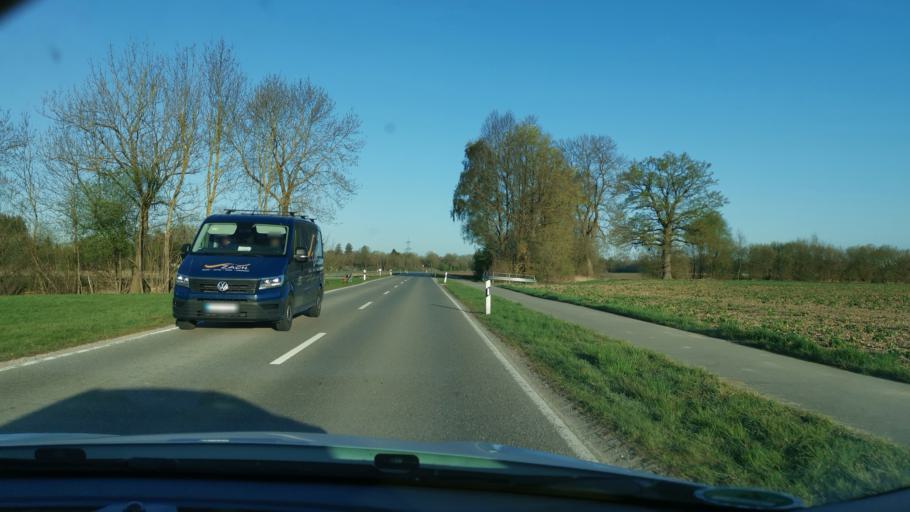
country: DE
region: Bavaria
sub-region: Swabia
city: Langweid
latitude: 48.4886
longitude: 10.8909
